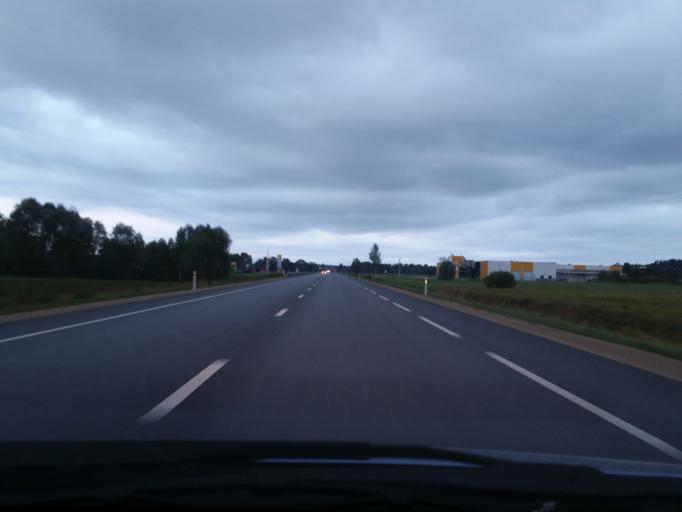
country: LV
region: Adazi
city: Adazi
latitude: 57.0920
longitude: 24.3126
